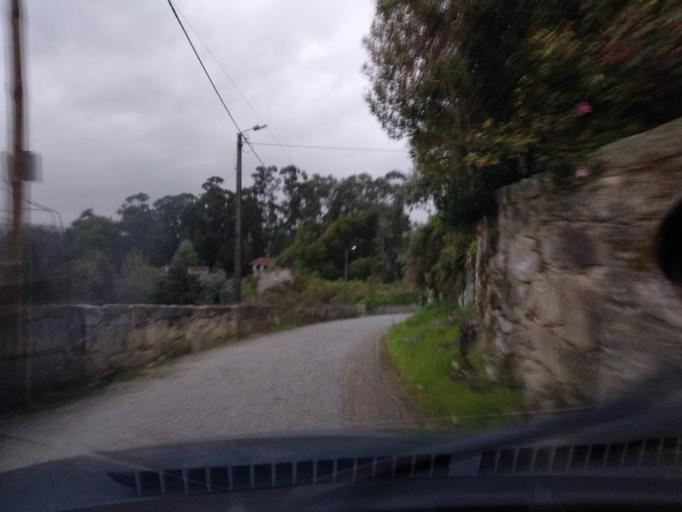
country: PT
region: Porto
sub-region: Penafiel
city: Penafiel
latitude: 41.1872
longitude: -8.2950
